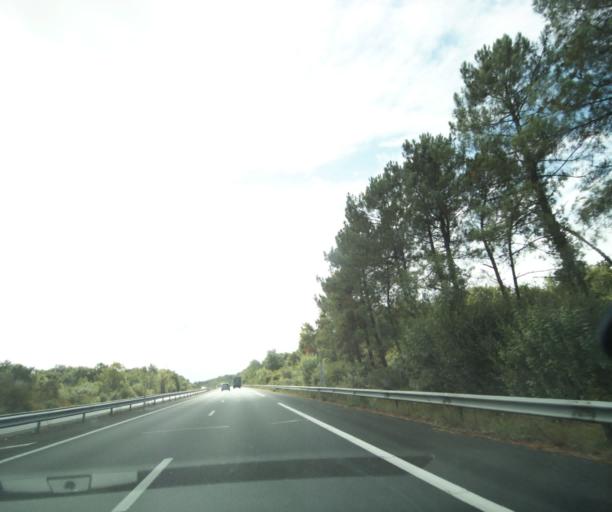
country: FR
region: Poitou-Charentes
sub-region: Departement de la Charente-Maritime
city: Thenac
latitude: 45.6478
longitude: -0.6316
